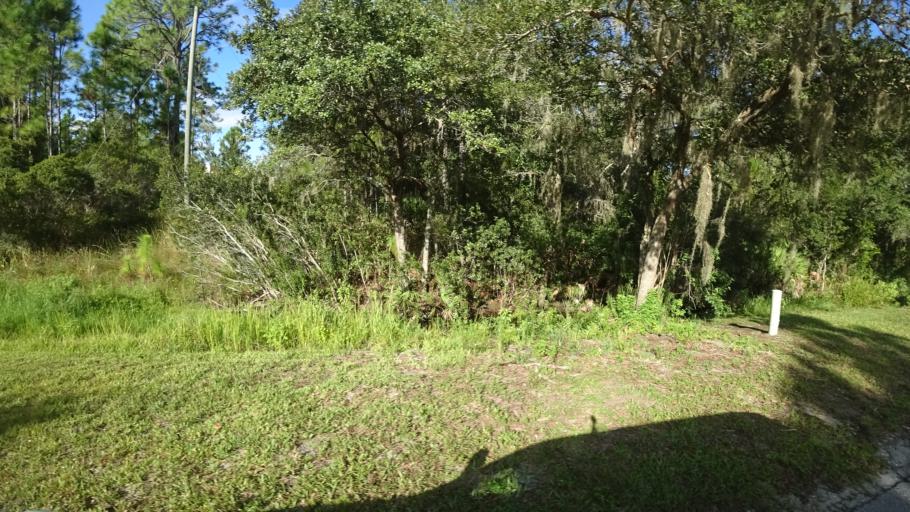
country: US
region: Florida
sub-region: Sarasota County
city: The Meadows
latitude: 27.4239
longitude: -82.3243
